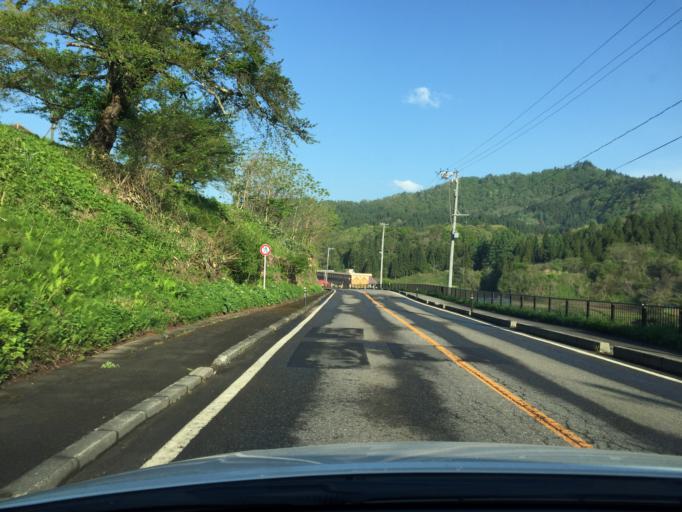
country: JP
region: Fukushima
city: Kitakata
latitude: 37.6683
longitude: 139.9769
